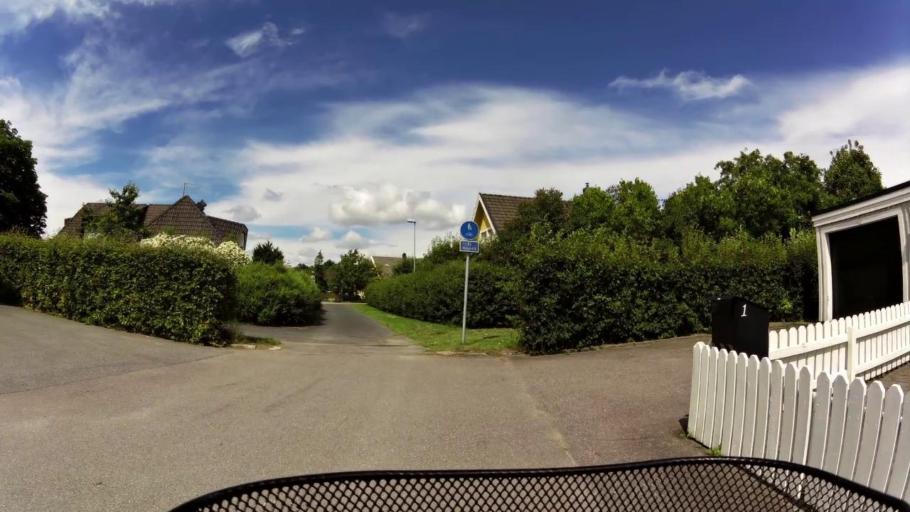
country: SE
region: OEstergoetland
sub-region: Linkopings Kommun
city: Malmslatt
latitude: 58.4267
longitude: 15.5183
